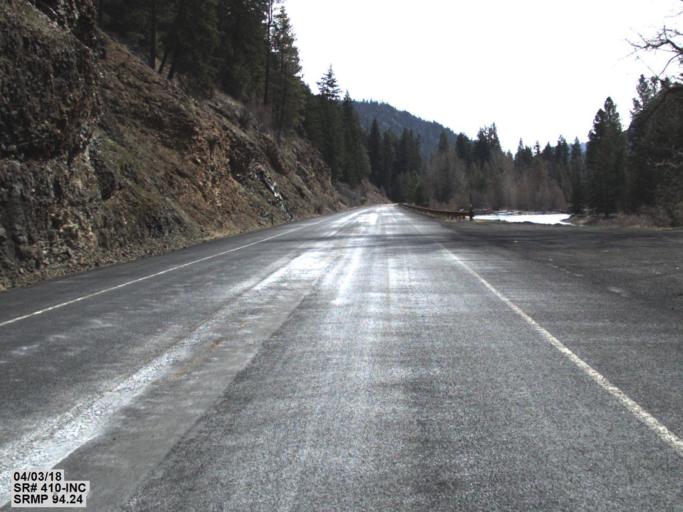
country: US
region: Washington
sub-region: Kittitas County
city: Cle Elum
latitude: 46.9639
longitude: -121.0857
